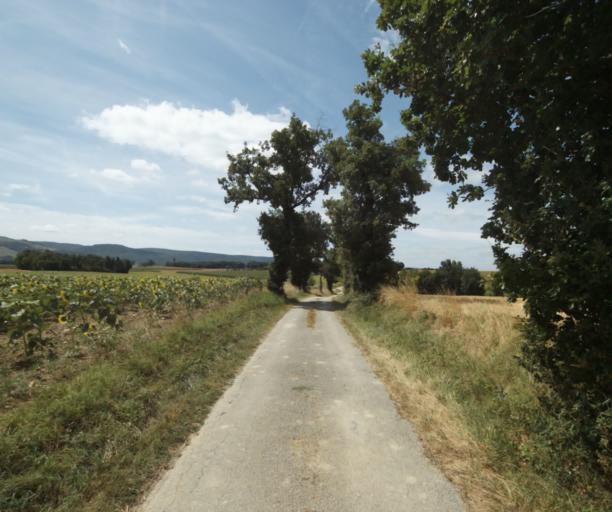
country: FR
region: Midi-Pyrenees
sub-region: Departement du Tarn
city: Soreze
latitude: 43.4870
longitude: 2.0709
